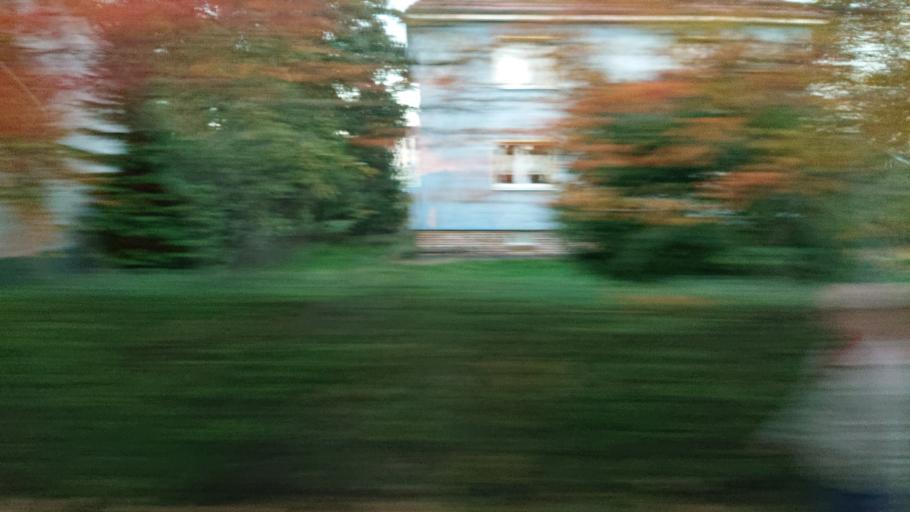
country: DE
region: Mecklenburg-Vorpommern
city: Greifswald
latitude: 54.0800
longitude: 13.3818
